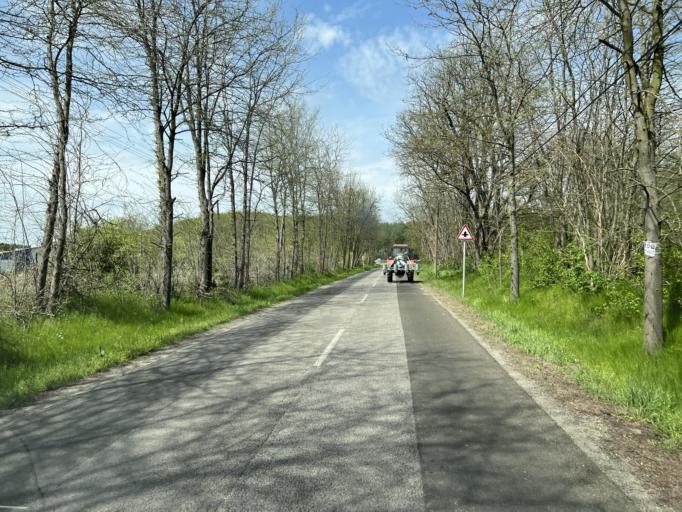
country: HU
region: Pest
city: Albertirsa
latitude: 47.2188
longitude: 19.6093
